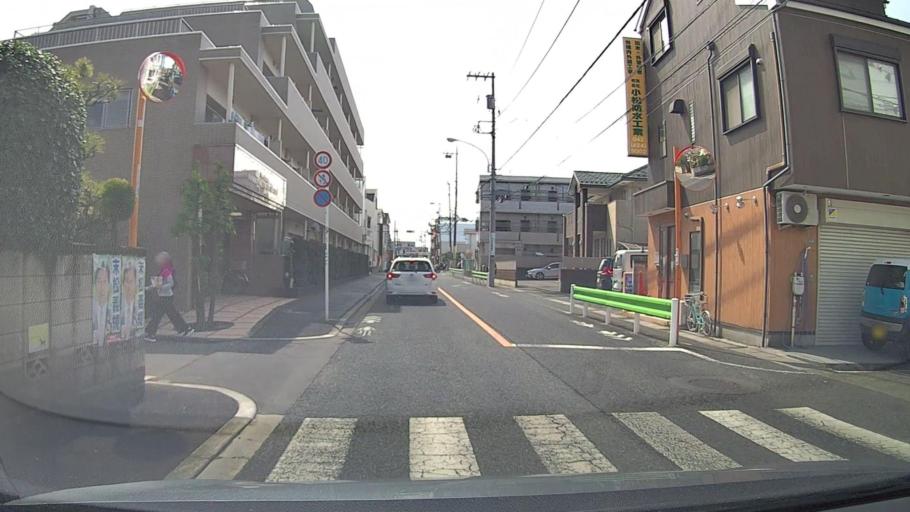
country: JP
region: Tokyo
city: Nishi-Tokyo-shi
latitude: 35.7410
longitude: 139.5526
